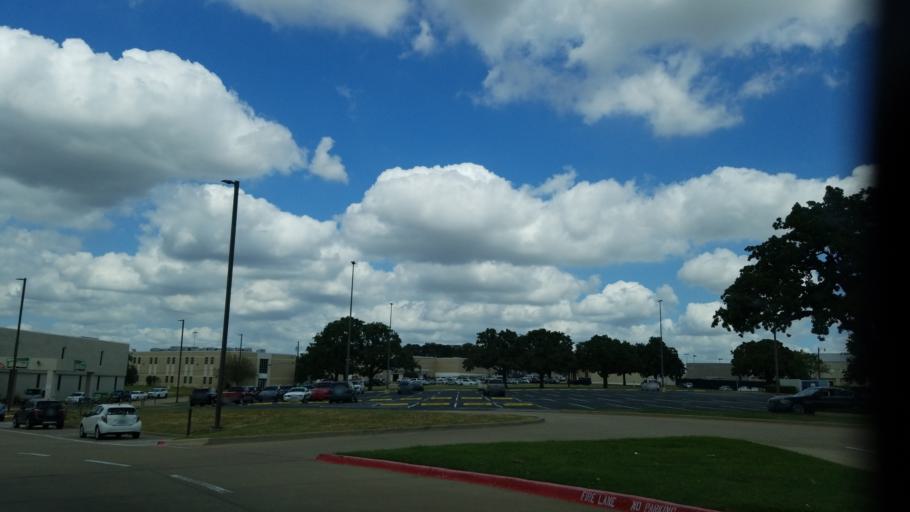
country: US
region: Texas
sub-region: Tarrant County
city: Euless
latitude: 32.8398
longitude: -97.0973
